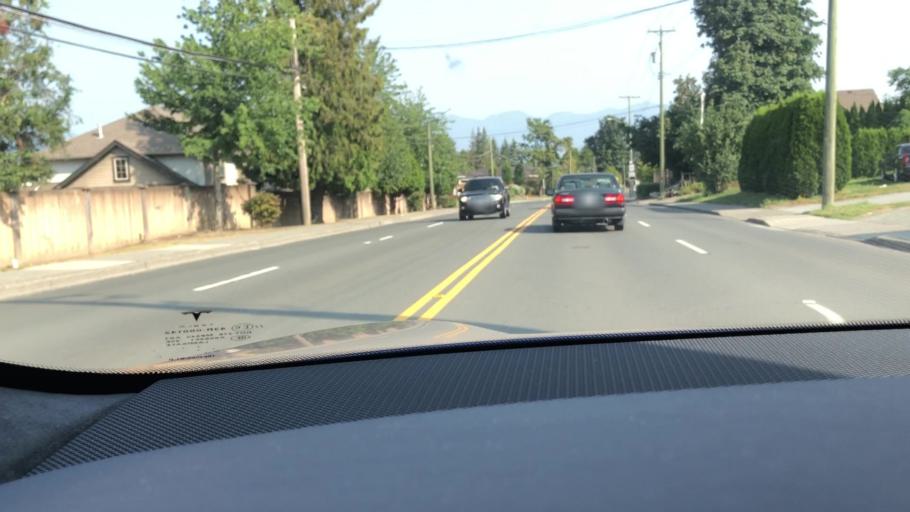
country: CA
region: British Columbia
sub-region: Fraser Valley Regional District
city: Chilliwack
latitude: 49.1201
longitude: -121.9593
